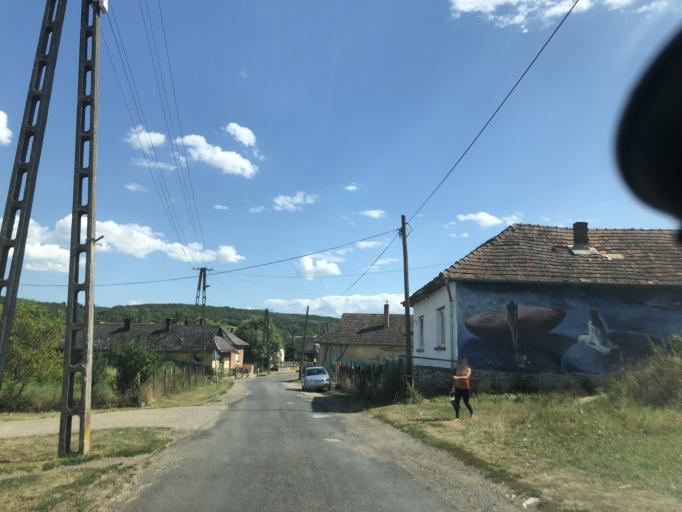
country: HU
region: Borsod-Abauj-Zemplen
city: Szendro
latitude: 48.5446
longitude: 20.8030
